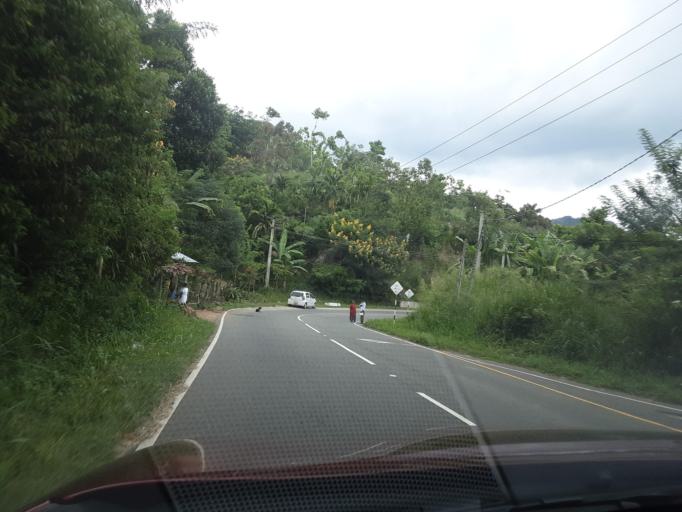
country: LK
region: Uva
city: Monaragala
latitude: 6.9068
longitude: 81.2096
